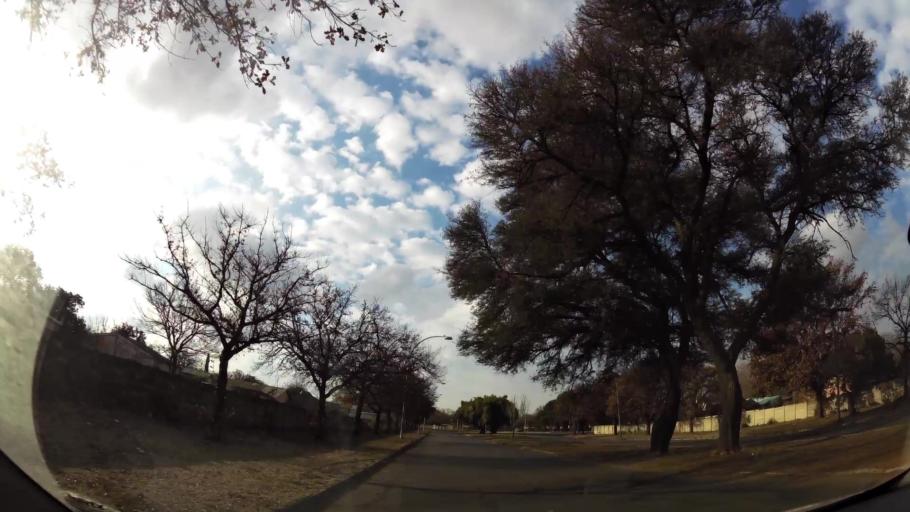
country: ZA
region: Orange Free State
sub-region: Fezile Dabi District Municipality
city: Sasolburg
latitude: -26.8183
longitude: 27.8092
